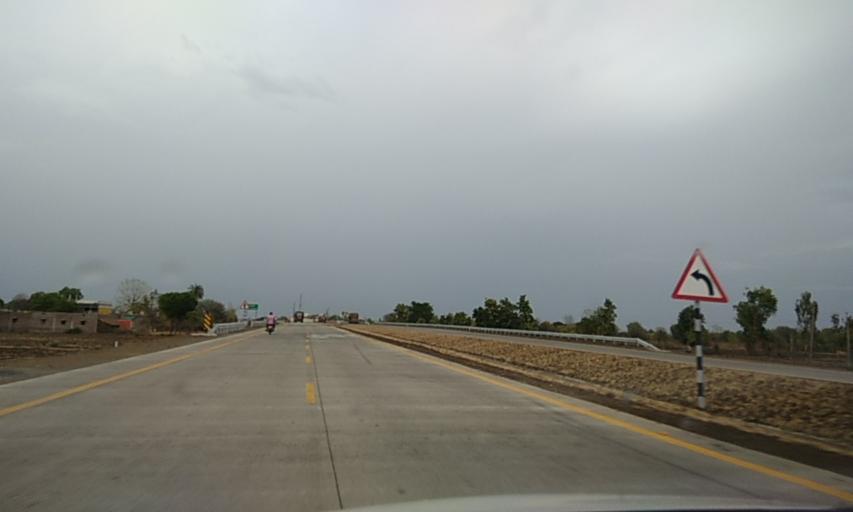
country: IN
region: Madhya Pradesh
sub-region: Rajgarh
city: Sarangpur
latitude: 23.6185
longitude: 76.5536
